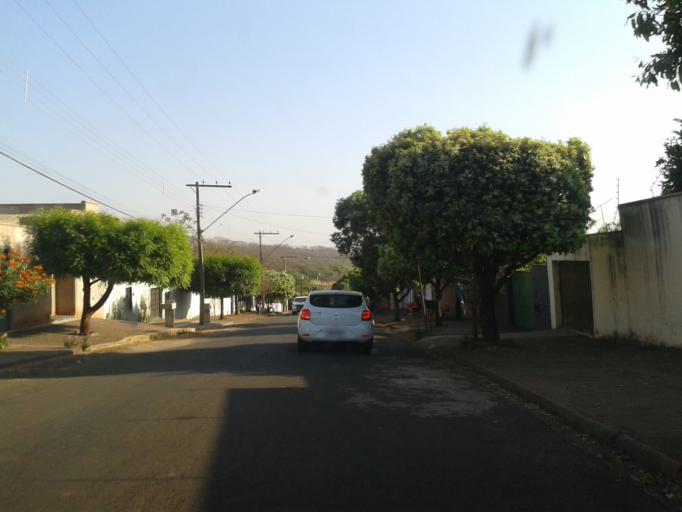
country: BR
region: Minas Gerais
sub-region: Ituiutaba
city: Ituiutaba
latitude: -18.9624
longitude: -49.4699
